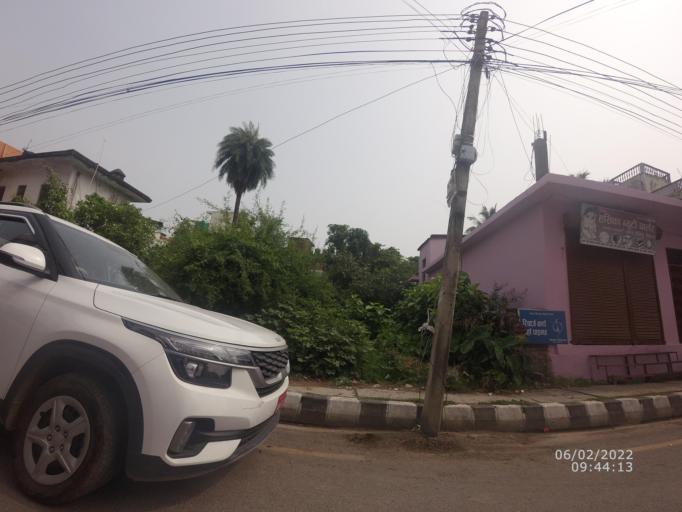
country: NP
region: Western Region
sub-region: Lumbini Zone
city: Bhairahawa
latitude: 27.5030
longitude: 83.4501
